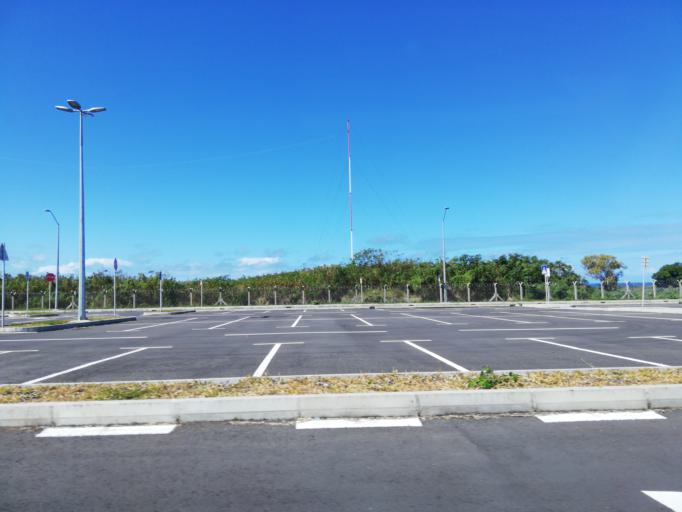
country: MU
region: Grand Port
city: Beau Vallon
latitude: -20.4410
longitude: 57.6898
